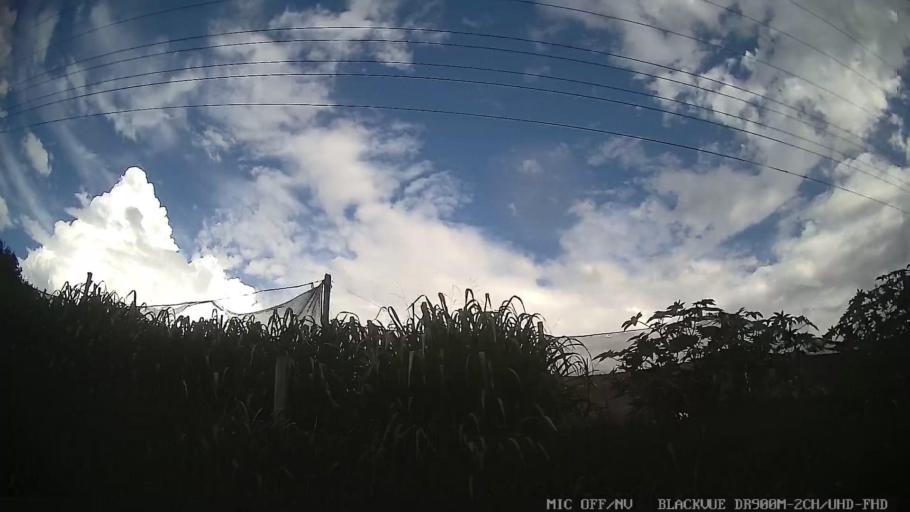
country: BR
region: Sao Paulo
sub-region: Jaguariuna
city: Jaguariuna
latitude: -22.6685
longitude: -47.0748
